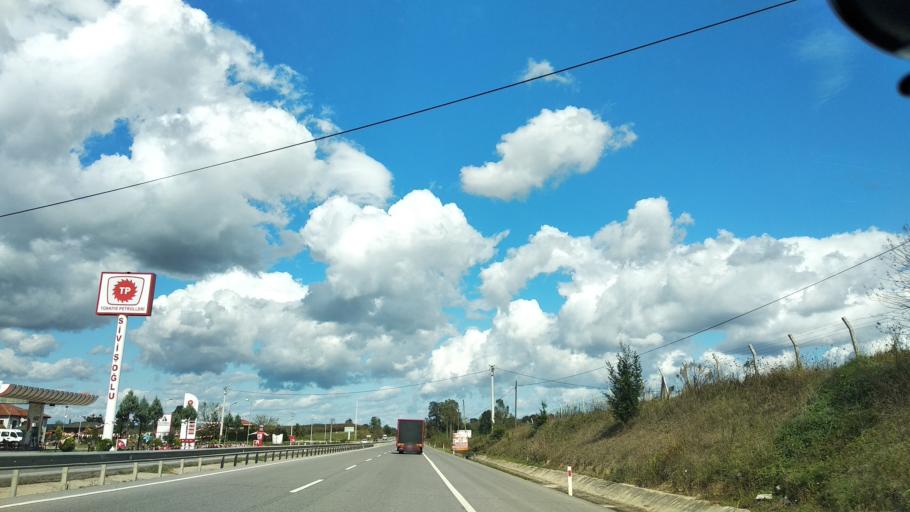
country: TR
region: Sakarya
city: Ferizli
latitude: 40.9725
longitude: 30.5104
